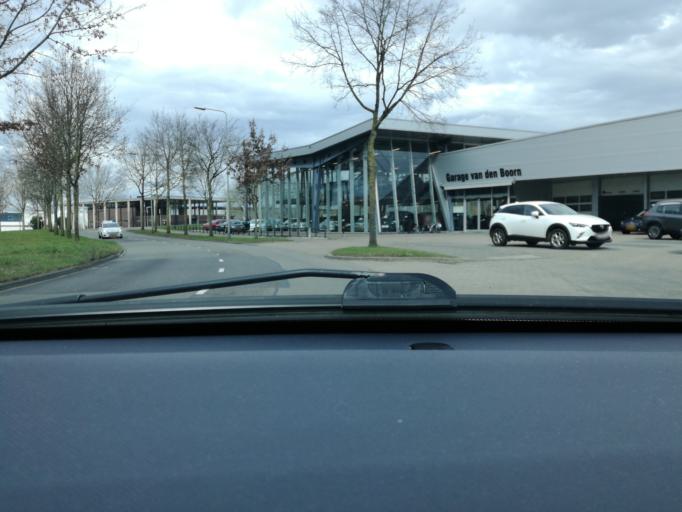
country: NL
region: Limburg
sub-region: Gemeente Maastricht
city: Heer
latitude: 50.8258
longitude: 5.7135
